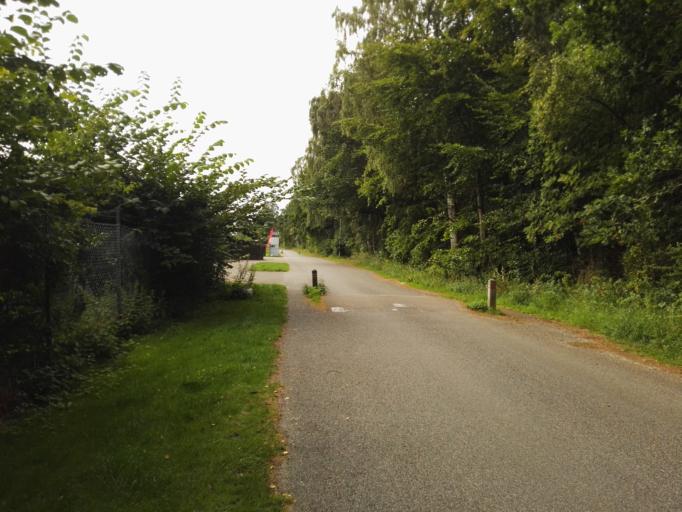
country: DK
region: Zealand
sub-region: Odsherred Kommune
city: Nykobing Sjaelland
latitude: 55.9422
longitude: 11.6833
